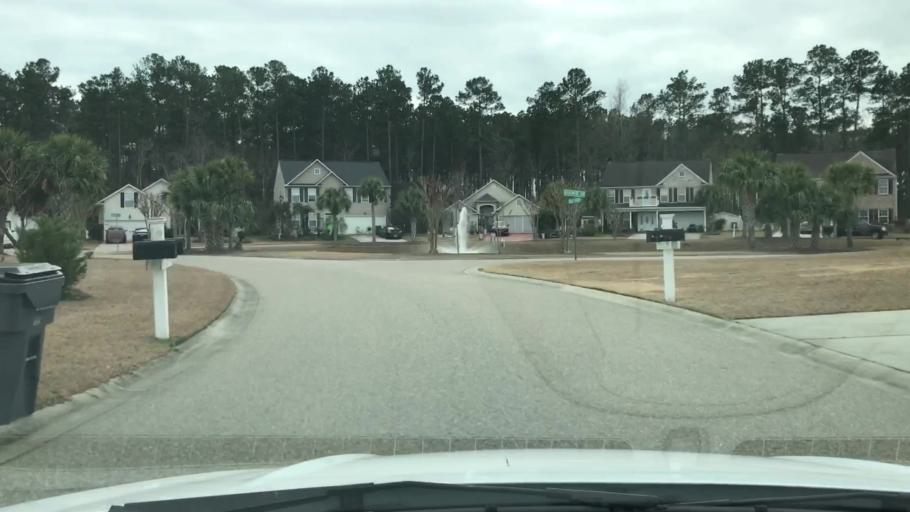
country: US
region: South Carolina
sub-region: Horry County
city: Socastee
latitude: 33.6700
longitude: -78.9741
